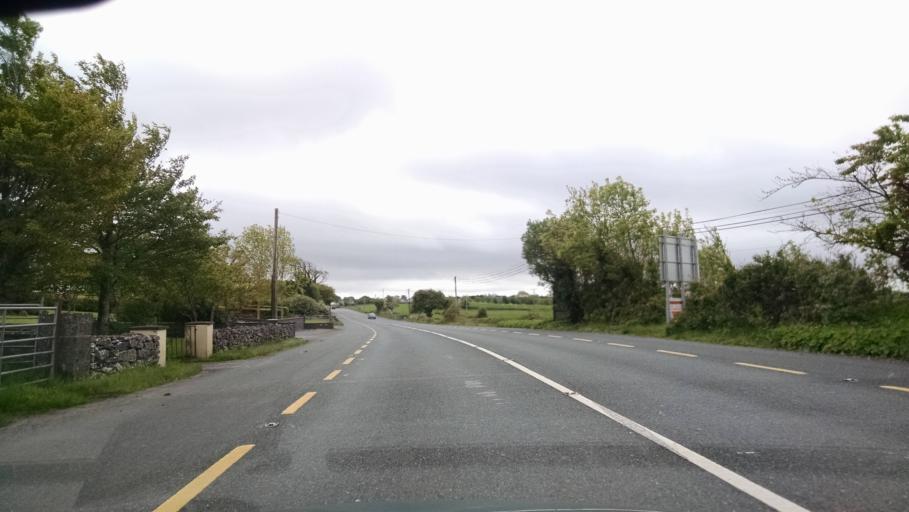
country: IE
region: Connaught
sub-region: County Galway
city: Moycullen
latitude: 53.4611
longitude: -9.1037
